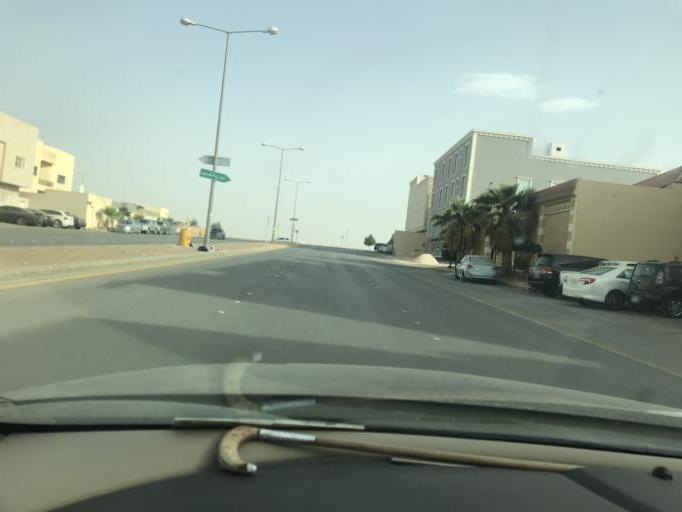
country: SA
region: Ar Riyad
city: Riyadh
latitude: 24.7821
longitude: 46.7154
